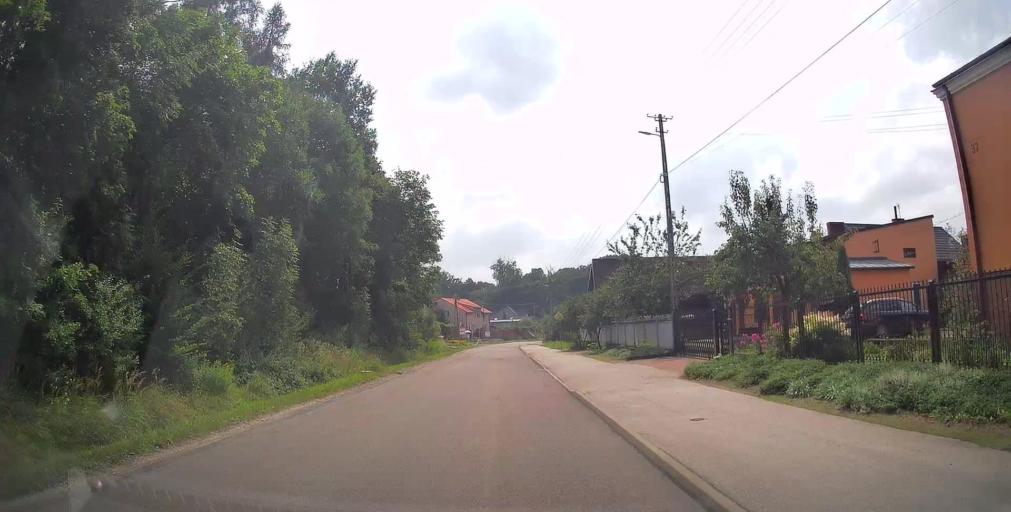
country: PL
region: Masovian Voivodeship
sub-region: Powiat bialobrzeski
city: Sucha
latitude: 51.6238
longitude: 20.9528
